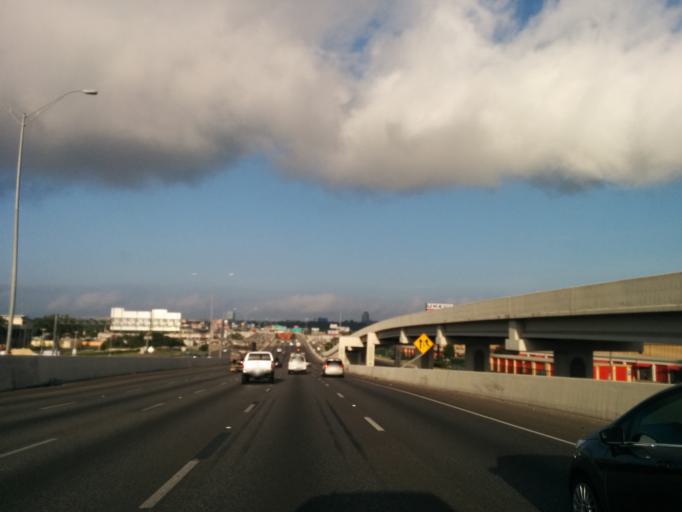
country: US
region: Texas
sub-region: Bexar County
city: Castle Hills
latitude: 29.5191
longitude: -98.5215
